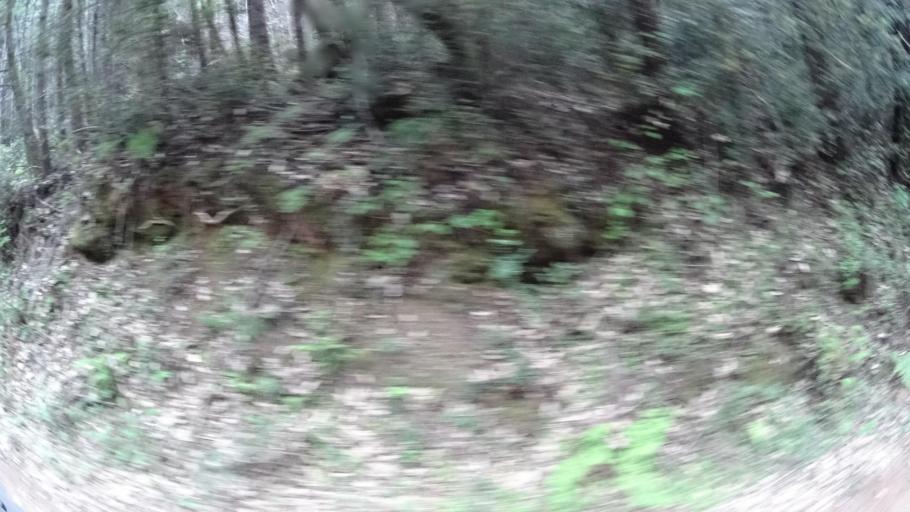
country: US
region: California
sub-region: Humboldt County
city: Willow Creek
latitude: 41.2009
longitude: -123.7554
